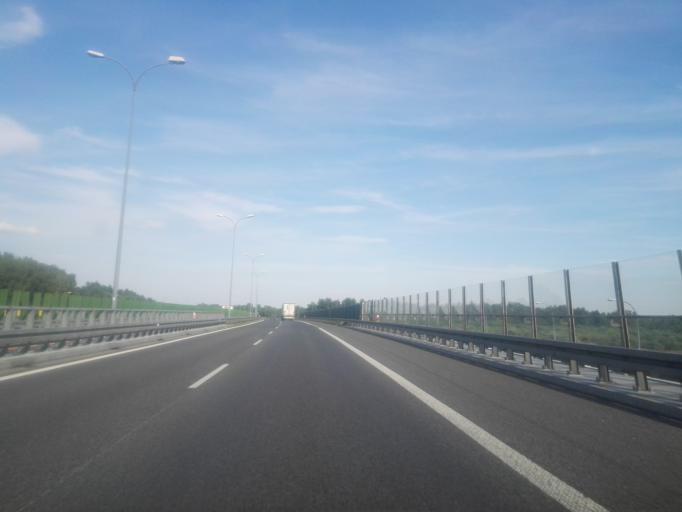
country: PL
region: Lower Silesian Voivodeship
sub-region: Powiat olesnicki
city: Olesnica
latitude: 51.2271
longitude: 17.4392
